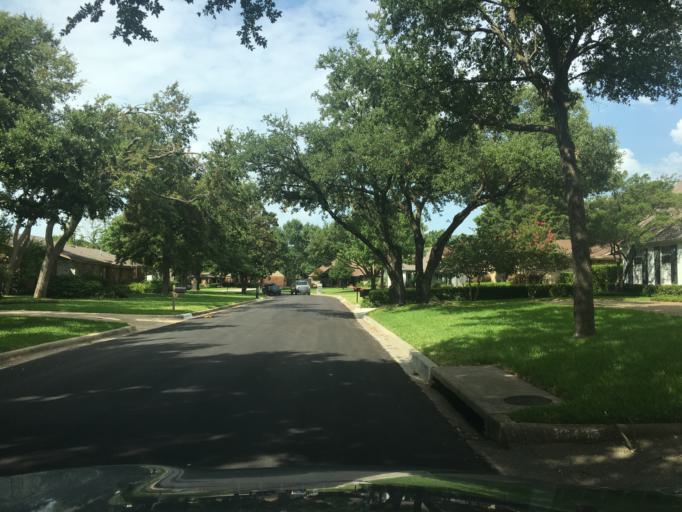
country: US
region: Texas
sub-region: Dallas County
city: Farmers Branch
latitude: 32.9295
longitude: -96.8627
